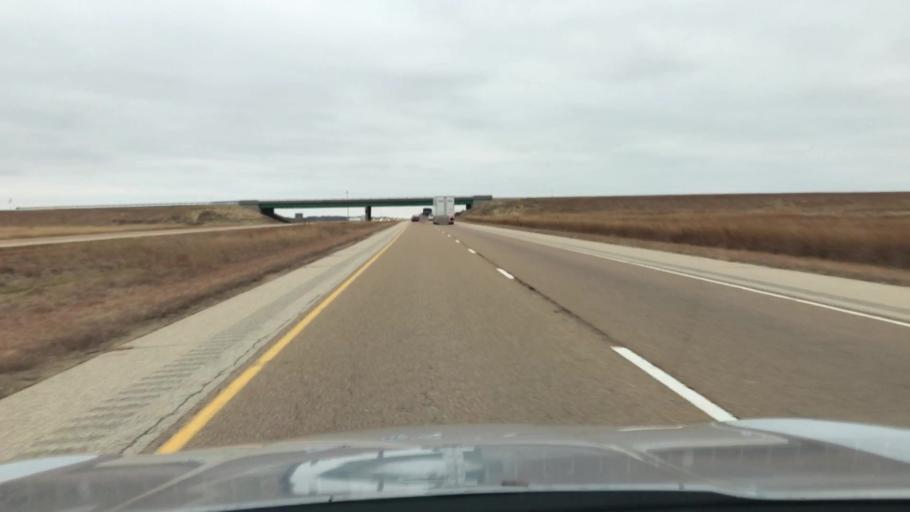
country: US
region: Illinois
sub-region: Montgomery County
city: Raymond
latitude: 39.3245
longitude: -89.6429
